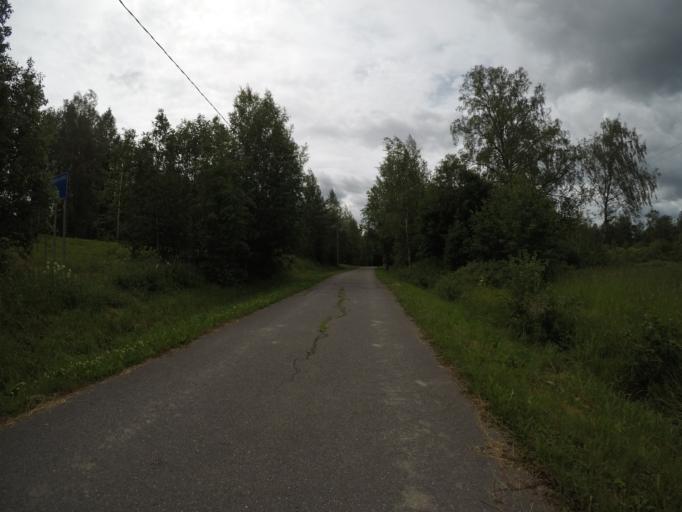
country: FI
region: Haeme
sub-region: Haemeenlinna
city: Haemeenlinna
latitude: 60.9979
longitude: 24.4969
